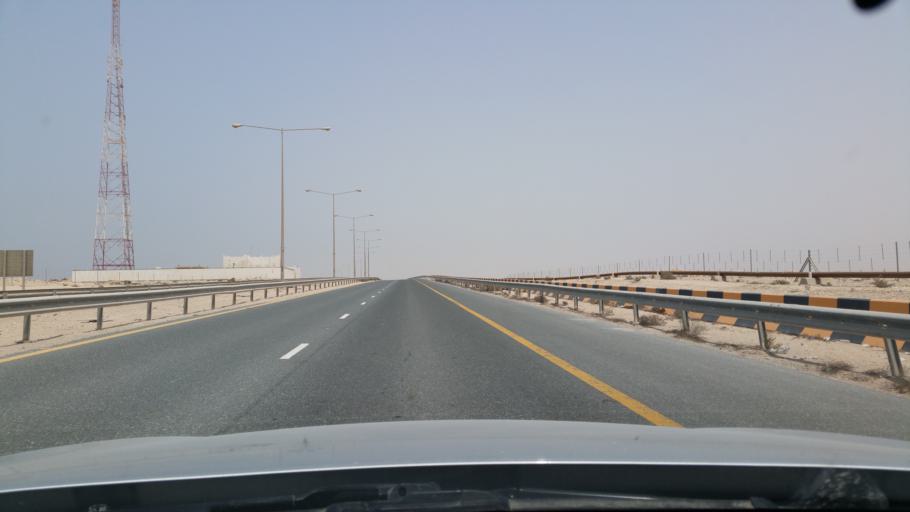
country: QA
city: Umm Bab
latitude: 25.3092
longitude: 50.7923
